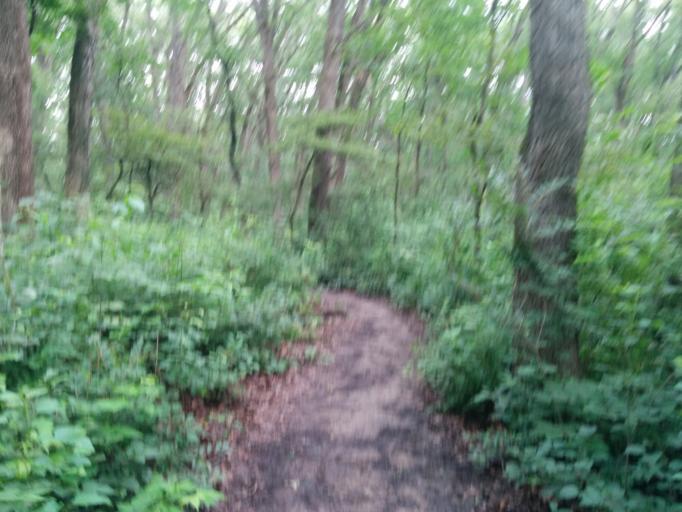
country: US
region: Illinois
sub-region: Cook County
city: Willow Springs
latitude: 41.7099
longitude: -87.8917
